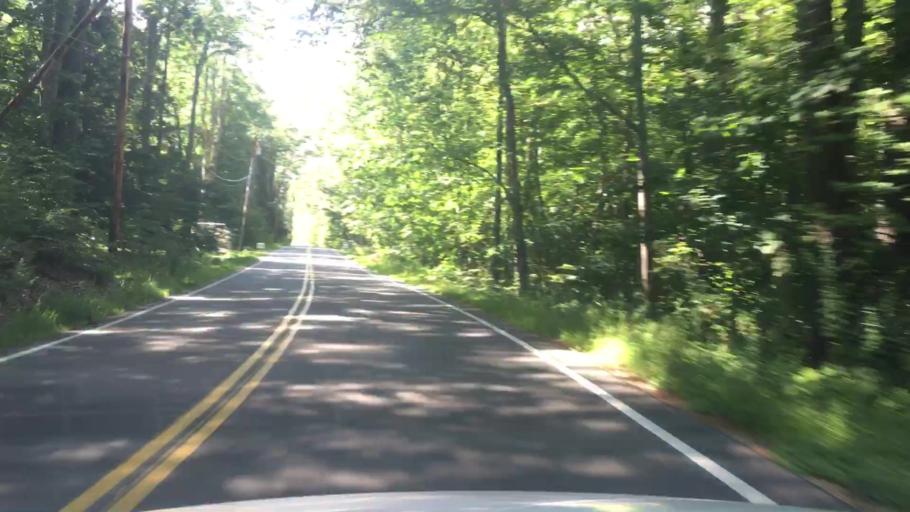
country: US
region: New Hampshire
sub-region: Strafford County
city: Dover
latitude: 43.1843
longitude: -70.8439
